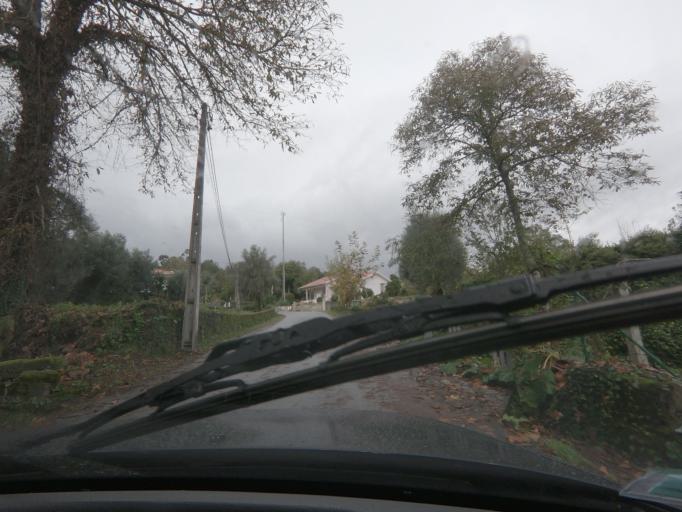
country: PT
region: Vila Real
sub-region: Mondim de Basto
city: Mondim de Basto
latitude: 41.3753
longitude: -7.9520
